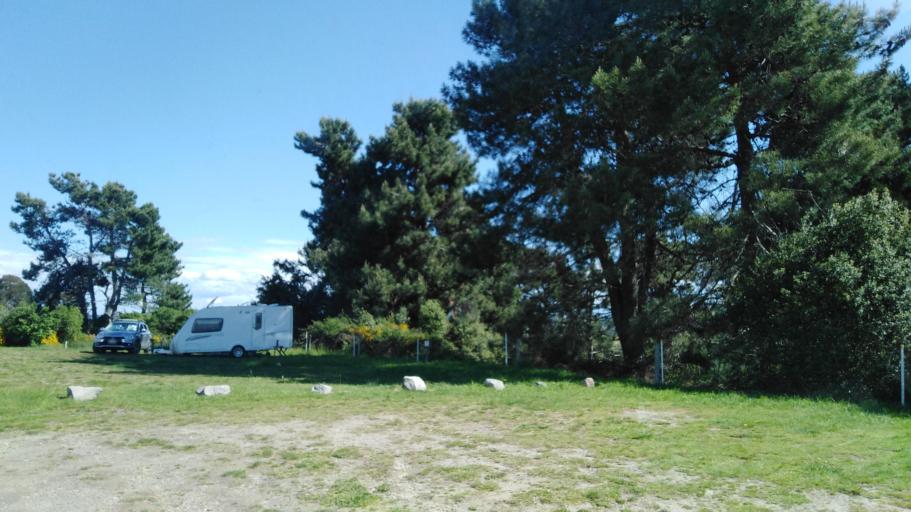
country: NZ
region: Waikato
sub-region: Taupo District
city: Taupo
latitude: -38.7395
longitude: 176.0802
